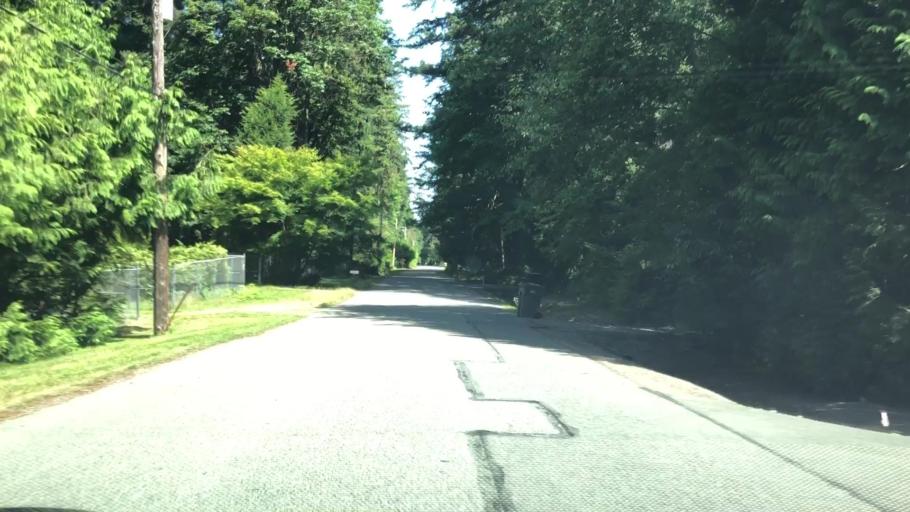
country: US
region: Washington
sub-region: Snohomish County
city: Maltby
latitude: 47.7727
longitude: -122.1184
